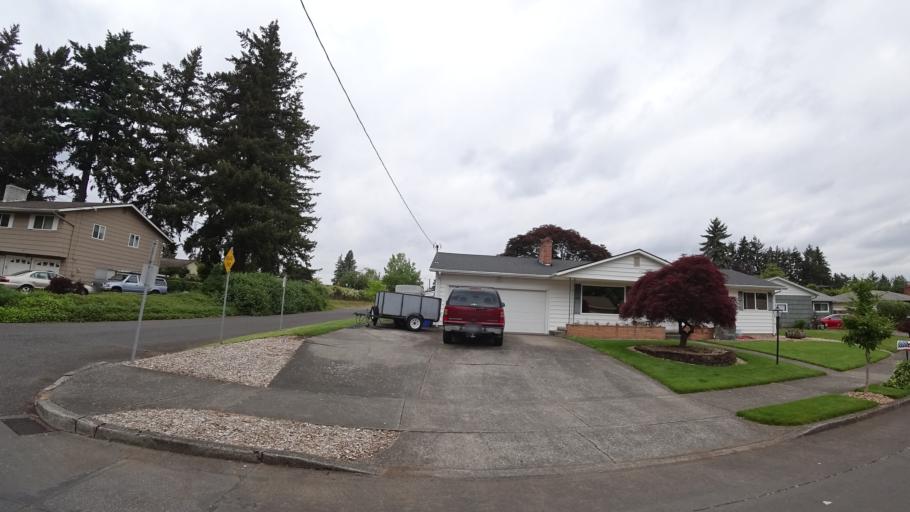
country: US
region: Oregon
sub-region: Multnomah County
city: Lents
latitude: 45.5130
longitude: -122.5324
